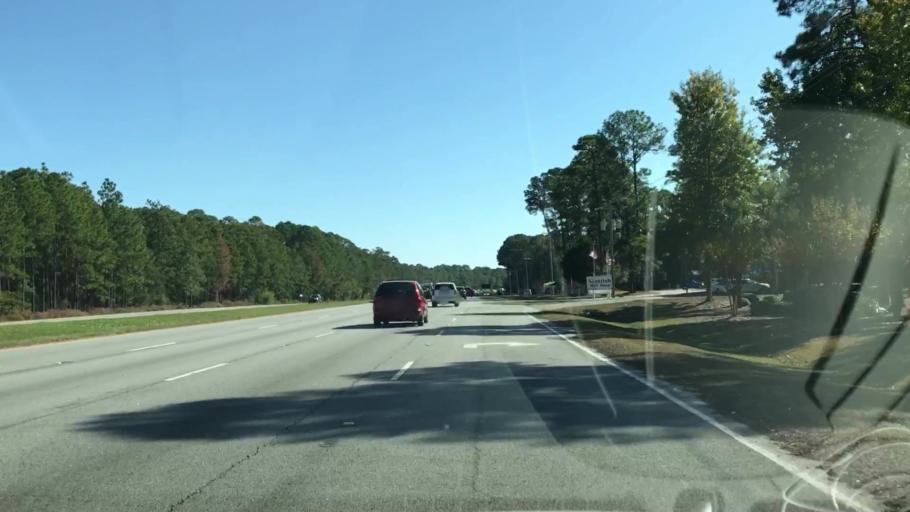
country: US
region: South Carolina
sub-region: Beaufort County
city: Bluffton
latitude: 32.2497
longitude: -80.8382
